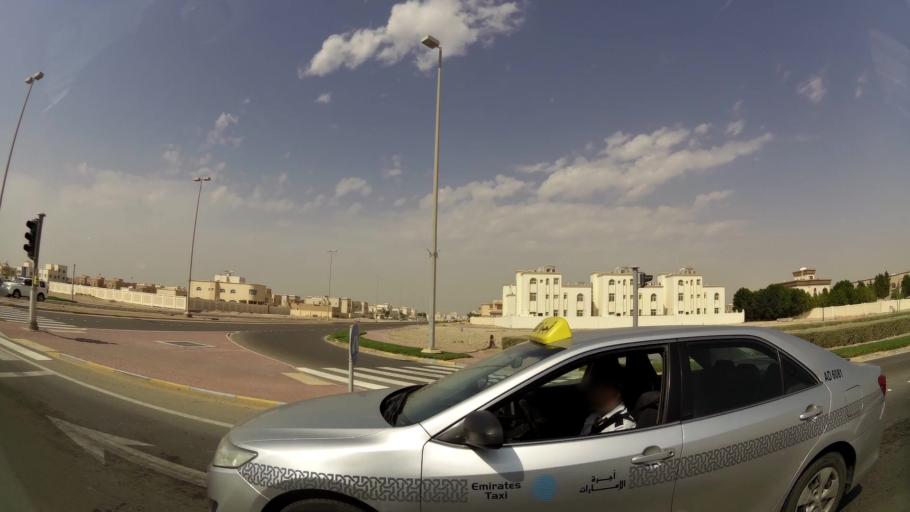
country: AE
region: Abu Dhabi
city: Abu Dhabi
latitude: 24.3253
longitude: 54.5523
